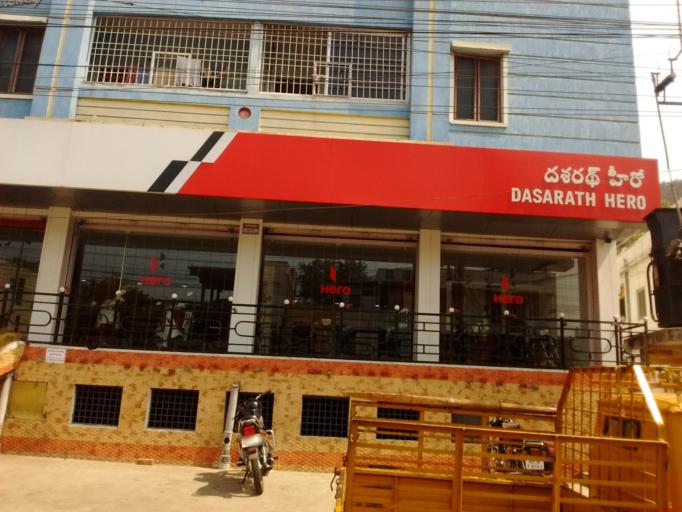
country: IN
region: Andhra Pradesh
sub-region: Krishna
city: Vijayawada
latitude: 16.5208
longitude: 80.6535
